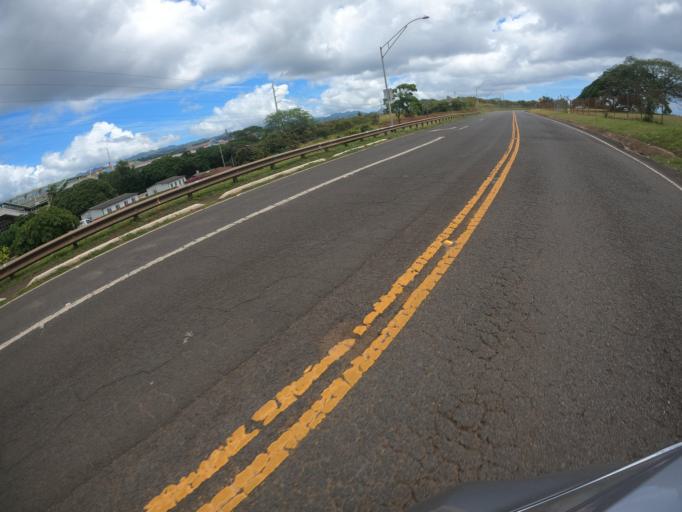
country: US
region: Hawaii
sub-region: Honolulu County
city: Pearl City, Manana
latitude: 21.3955
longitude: -157.9812
